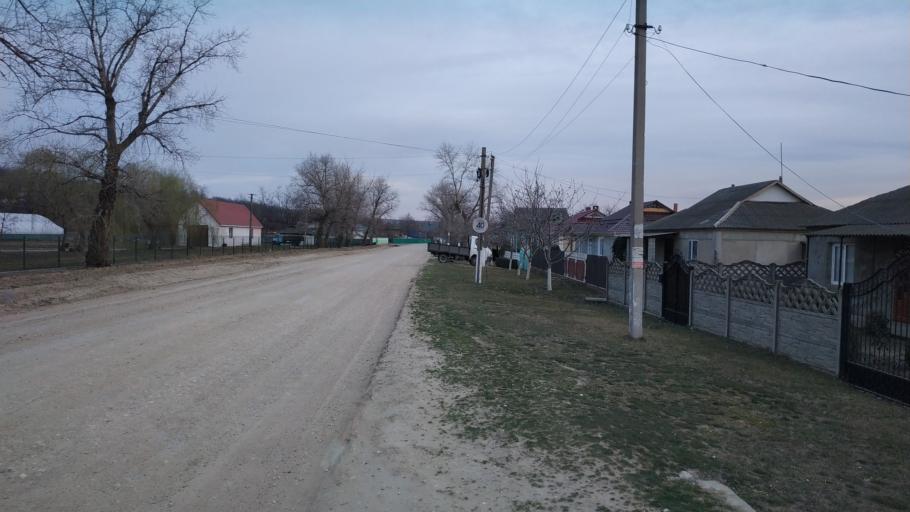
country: MD
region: Hincesti
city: Dancu
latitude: 46.7414
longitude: 28.2109
